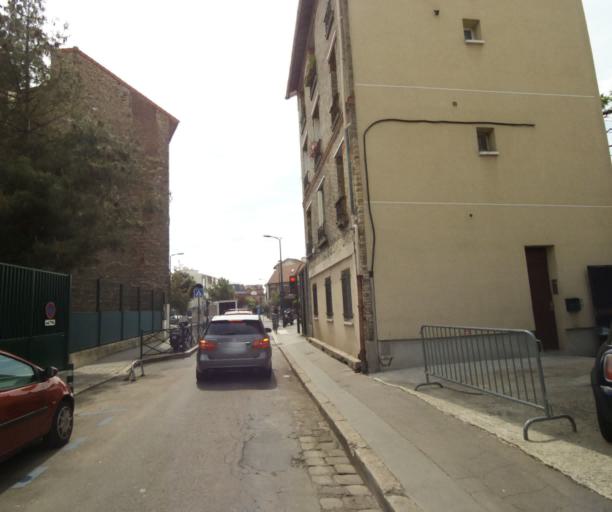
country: FR
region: Ile-de-France
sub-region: Departement des Hauts-de-Seine
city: Bois-Colombes
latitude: 48.9283
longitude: 2.2680
